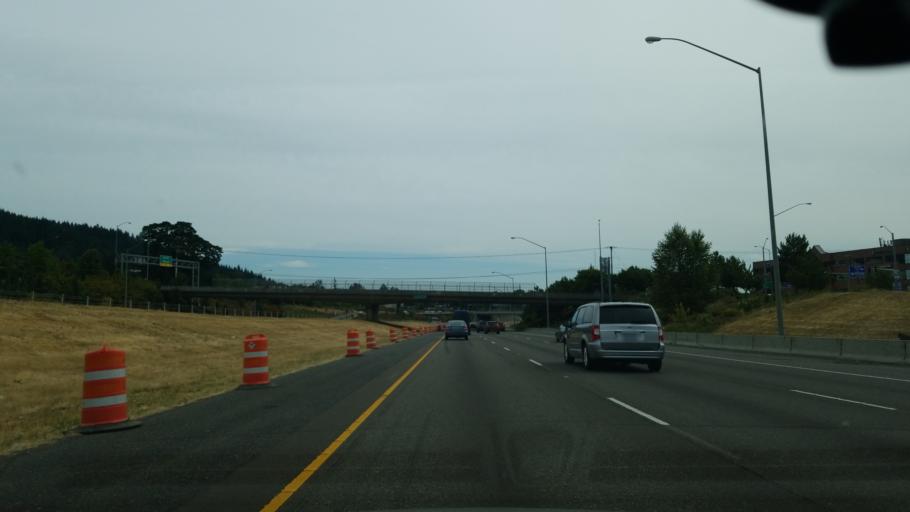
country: US
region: Oregon
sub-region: Clackamas County
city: Clackamas
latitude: 45.4347
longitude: -122.5669
